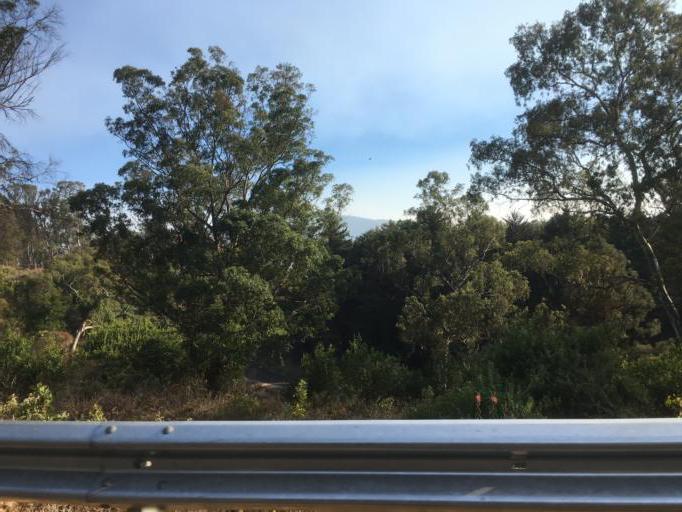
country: MX
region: Michoacan
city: Santa Fe de la Laguna
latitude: 19.6794
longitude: -101.5755
